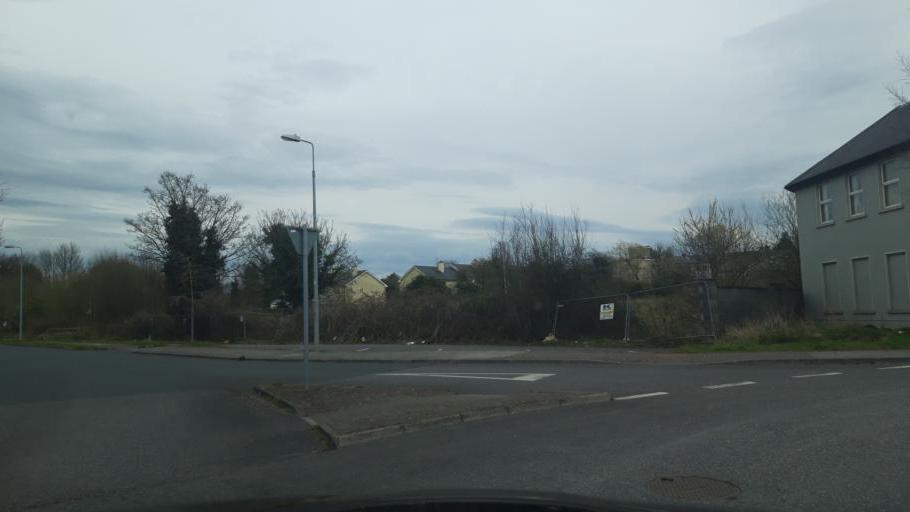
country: IE
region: Leinster
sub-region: Uibh Fhaili
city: Edenderry
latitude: 53.3424
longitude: -7.0571
